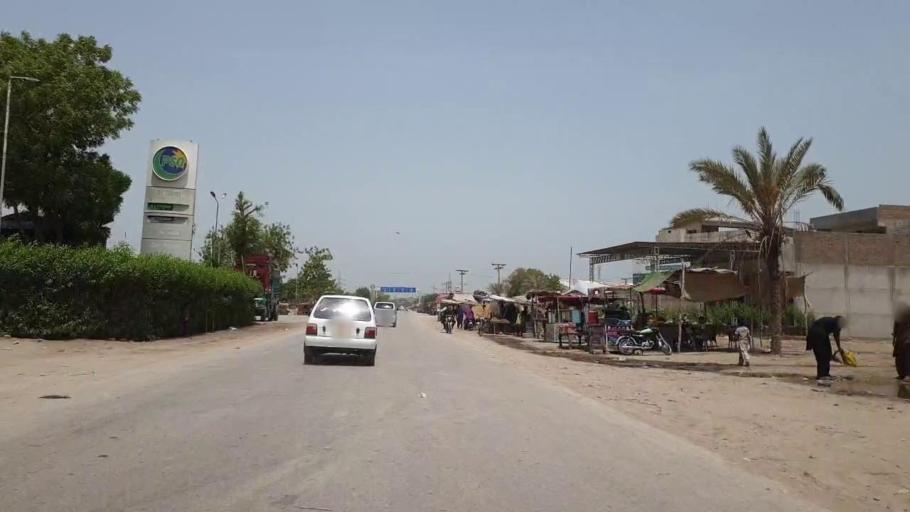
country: PK
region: Sindh
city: Nawabshah
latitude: 26.2473
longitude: 68.4317
